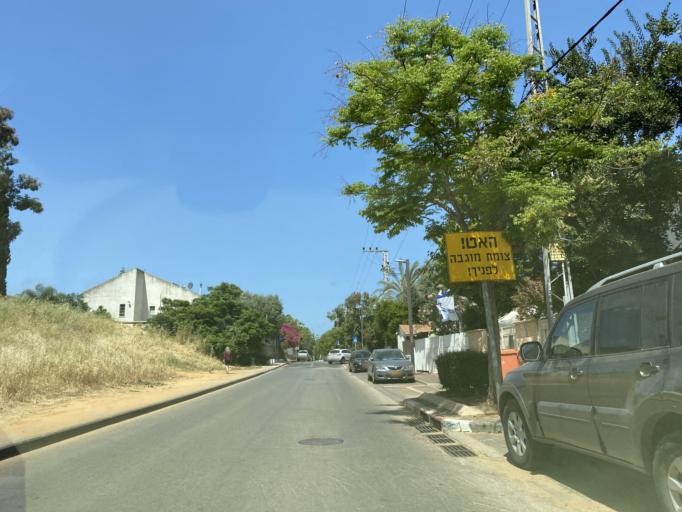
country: IL
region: Tel Aviv
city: Ramat HaSharon
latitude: 32.1534
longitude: 34.8369
